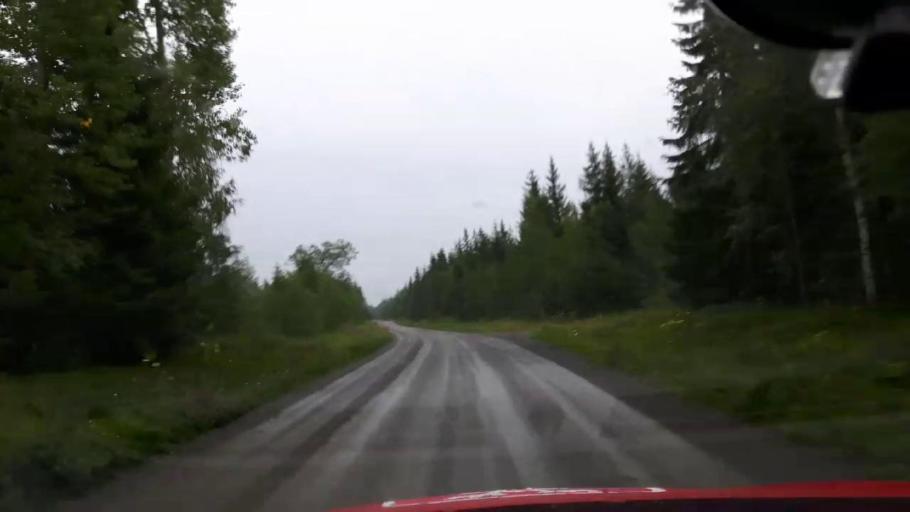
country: SE
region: Jaemtland
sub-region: OEstersunds Kommun
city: Brunflo
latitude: 62.9752
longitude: 14.8318
